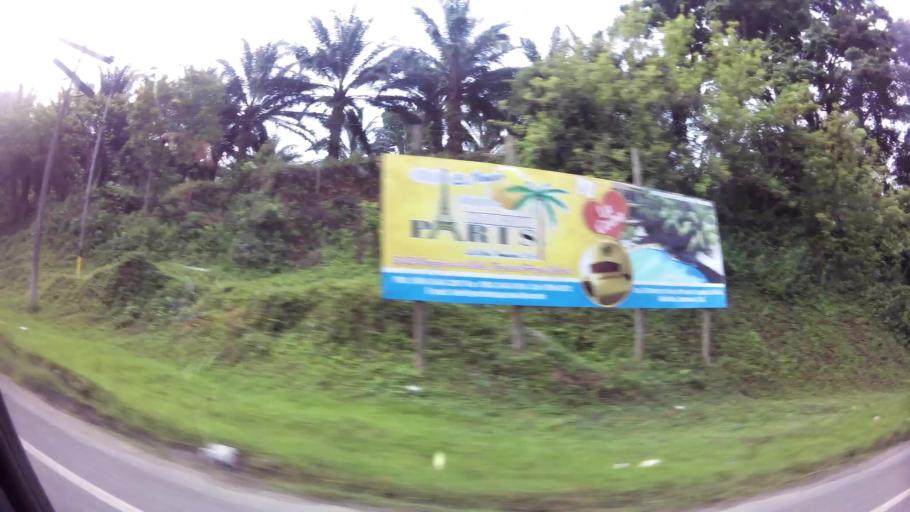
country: HN
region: Yoro
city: Toyos
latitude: 15.5134
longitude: -87.6658
